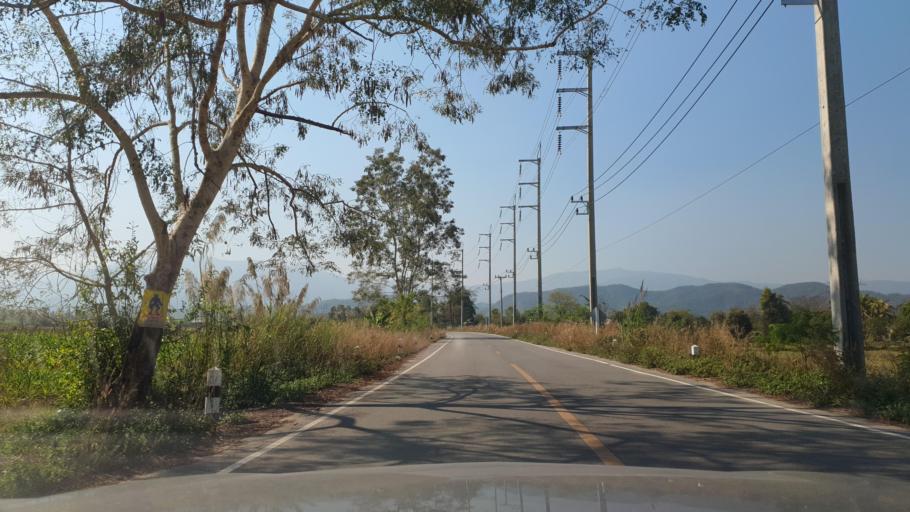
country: TH
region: Chiang Rai
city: Mae Lao
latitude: 19.8022
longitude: 99.6953
